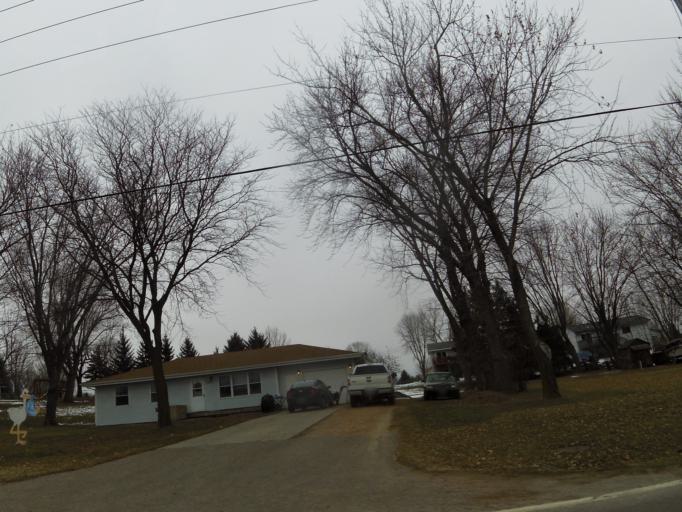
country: US
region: Minnesota
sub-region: Carver County
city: Cologne
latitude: 44.7770
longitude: -93.7851
